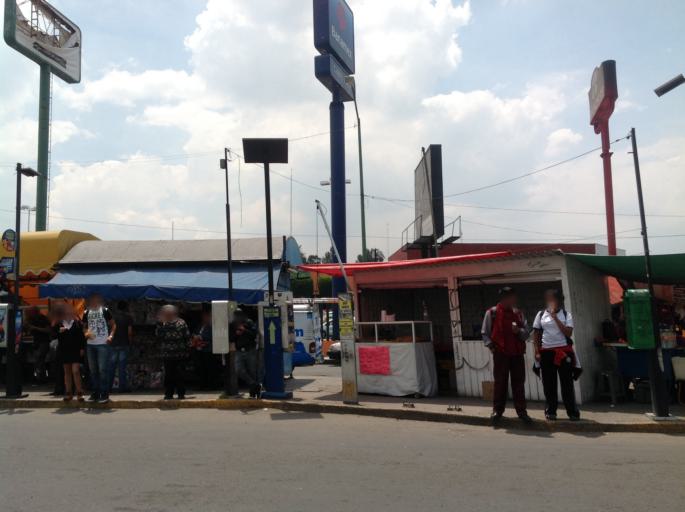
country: MX
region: Mexico
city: Cuautitlan Izcalli
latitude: 19.6071
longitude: -99.2282
